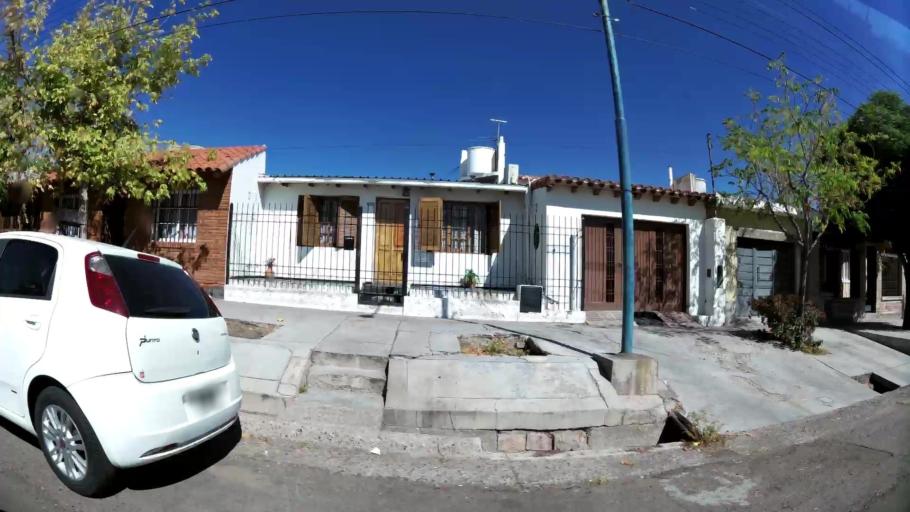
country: AR
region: Mendoza
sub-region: Departamento de Godoy Cruz
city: Godoy Cruz
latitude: -32.9158
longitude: -68.8791
